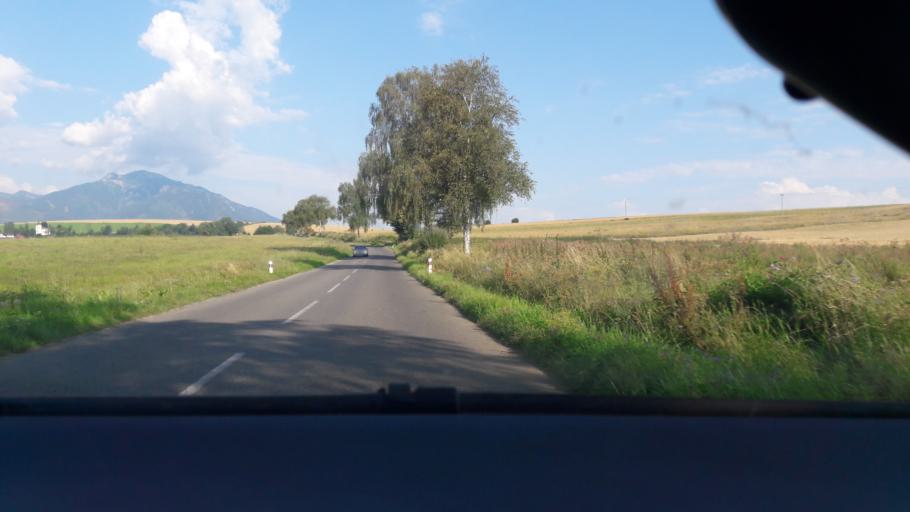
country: SK
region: Presovsky
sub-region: Okres Presov
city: Kezmarok
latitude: 49.1844
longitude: 20.3957
